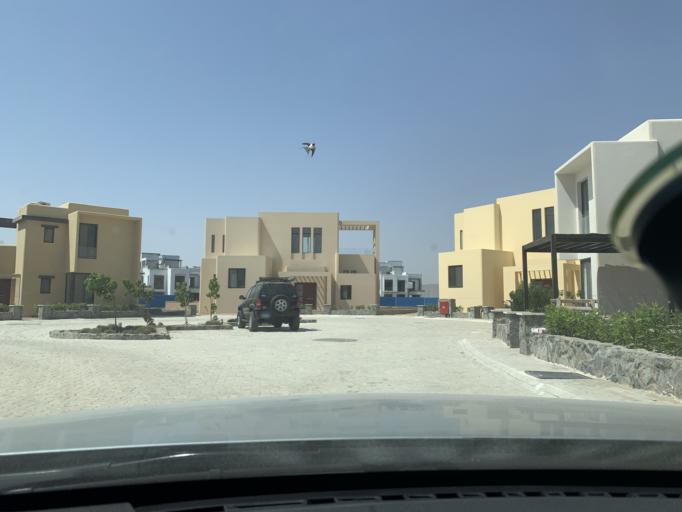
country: EG
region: Red Sea
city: El Gouna
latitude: 27.4018
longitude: 33.6593
